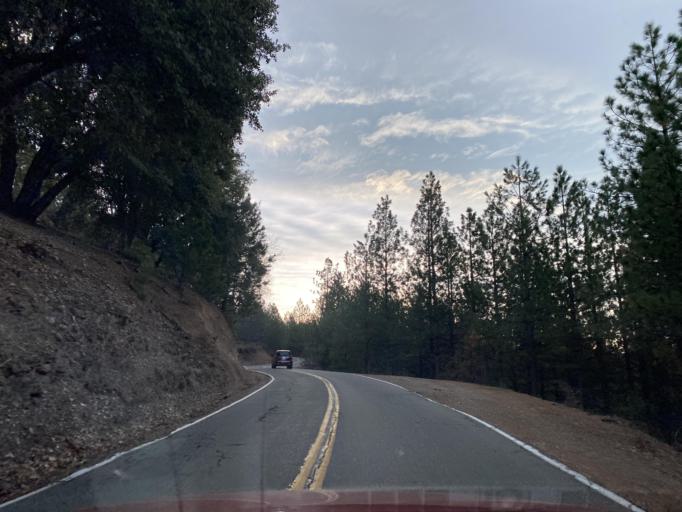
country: US
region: California
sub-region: Amador County
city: Pioneer
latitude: 38.4977
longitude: -120.5981
